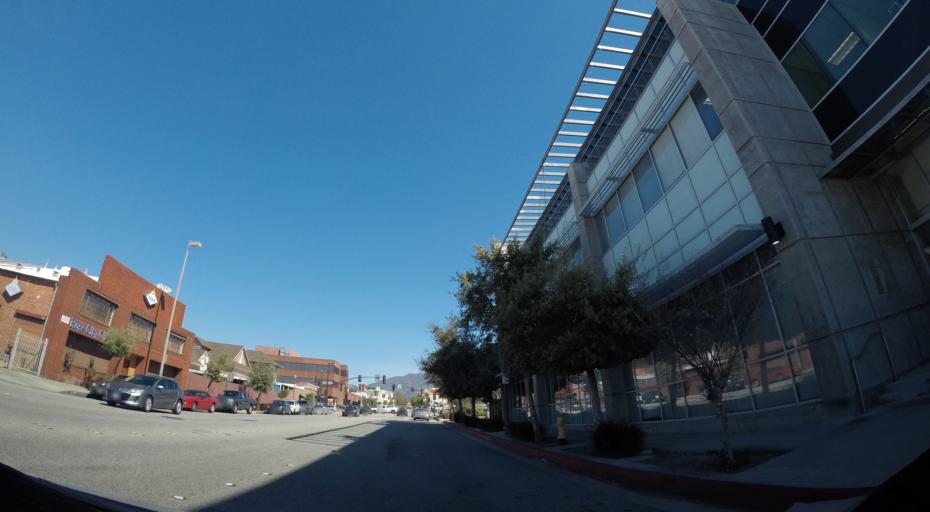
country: US
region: California
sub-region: Los Angeles County
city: Pasadena
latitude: 34.1349
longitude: -118.1488
